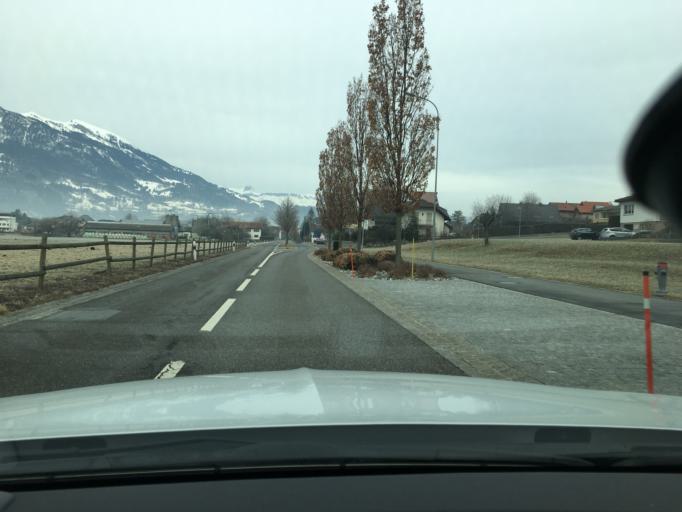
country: LI
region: Balzers
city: Balzers
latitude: 47.0620
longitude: 9.5098
